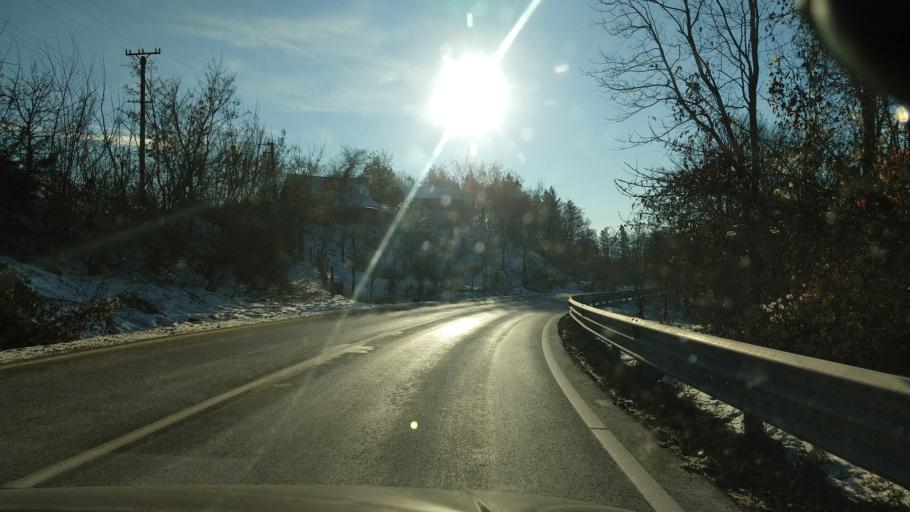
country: RO
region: Bacau
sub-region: Comuna Luizi-Calugara
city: Luizi-Calugara
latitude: 46.4963
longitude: 26.7963
